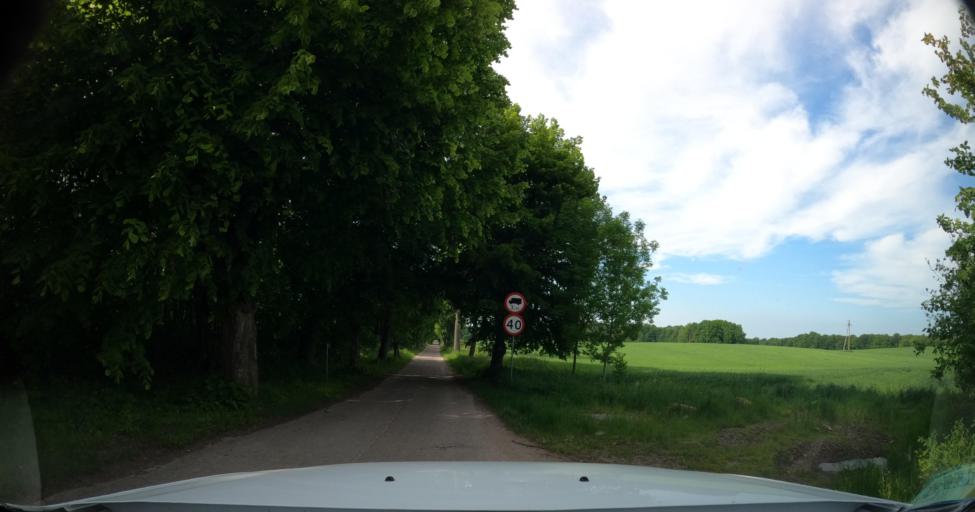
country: PL
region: Warmian-Masurian Voivodeship
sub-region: Powiat ostrodzki
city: Morag
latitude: 54.0203
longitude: 19.9143
